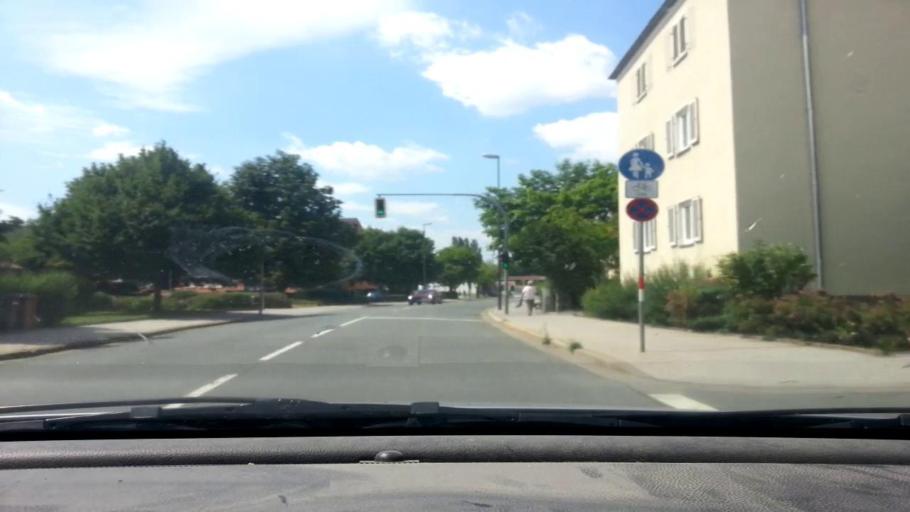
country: DE
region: Bavaria
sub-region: Upper Franconia
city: Bayreuth
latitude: 49.9458
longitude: 11.5942
